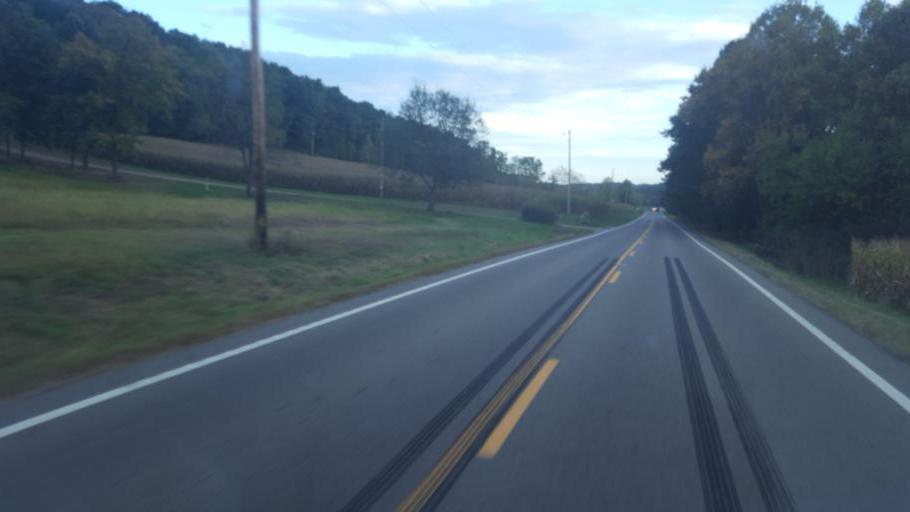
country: US
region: Ohio
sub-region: Ashland County
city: Loudonville
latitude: 40.6829
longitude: -82.2378
